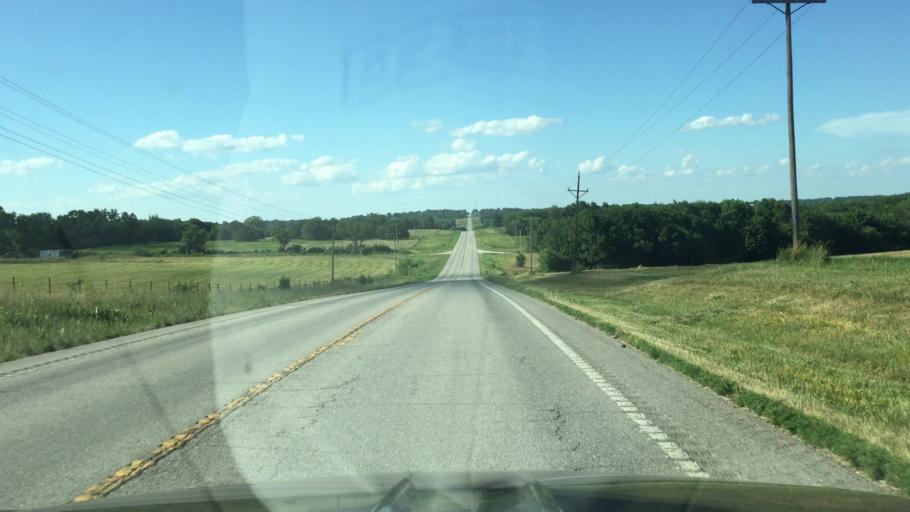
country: US
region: Missouri
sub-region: Morgan County
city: Versailles
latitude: 38.5380
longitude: -92.7980
